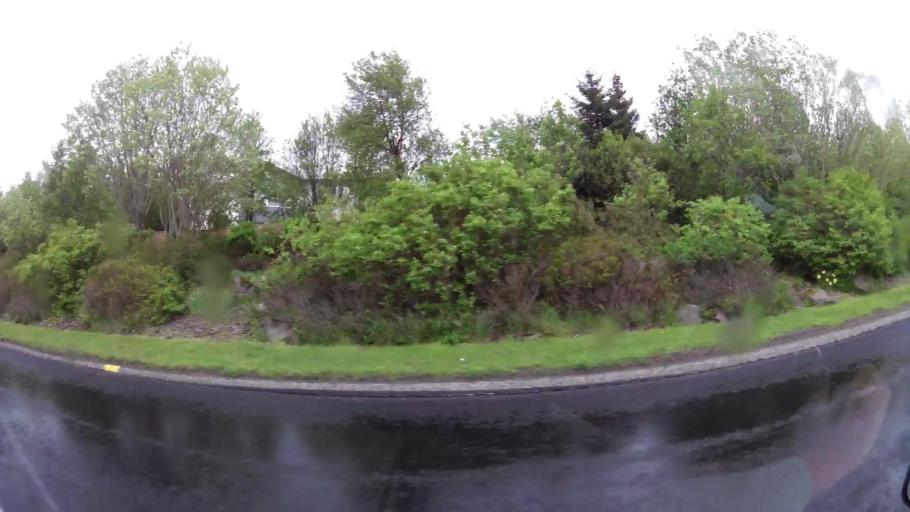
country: IS
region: Capital Region
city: Kopavogur
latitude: 64.0966
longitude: -21.9035
